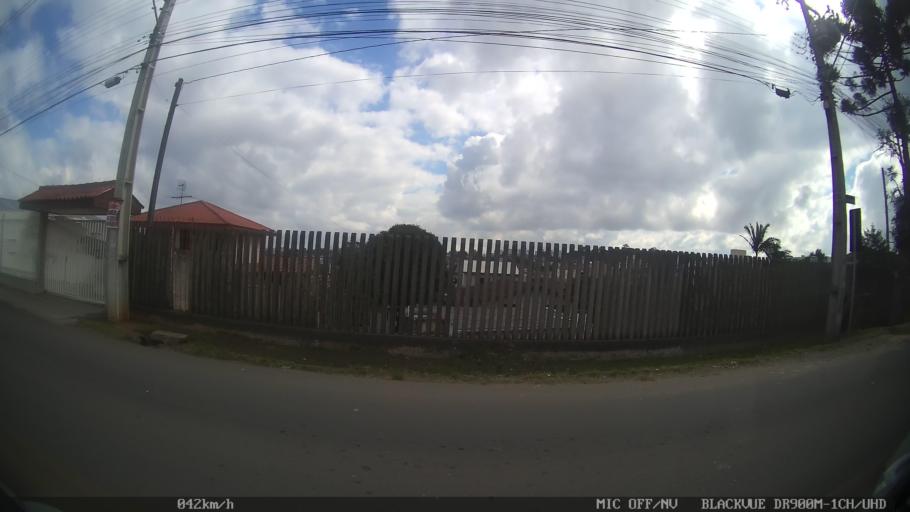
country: BR
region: Parana
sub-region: Colombo
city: Colombo
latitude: -25.3488
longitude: -49.2042
